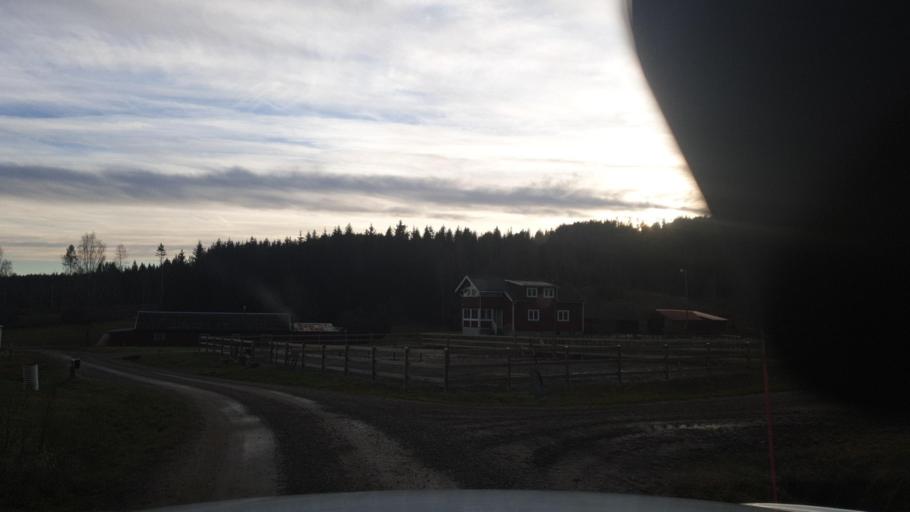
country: NO
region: Ostfold
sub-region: Romskog
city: Romskog
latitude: 59.8132
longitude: 11.9959
